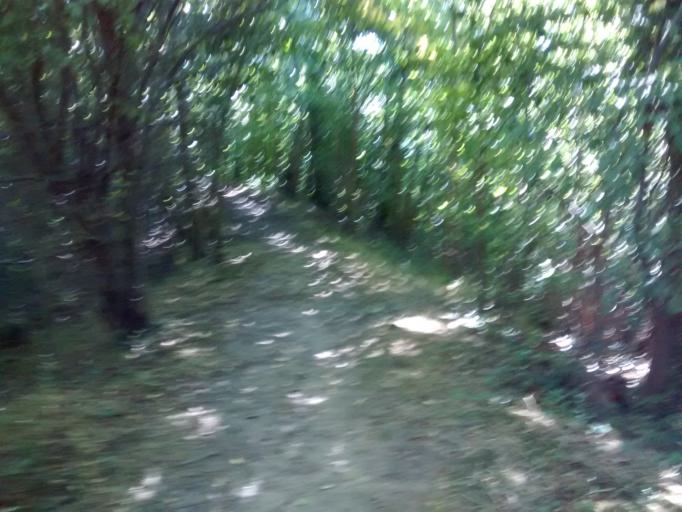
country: DK
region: Zealand
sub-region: Soro Kommune
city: Soro
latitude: 55.4524
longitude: 11.5537
